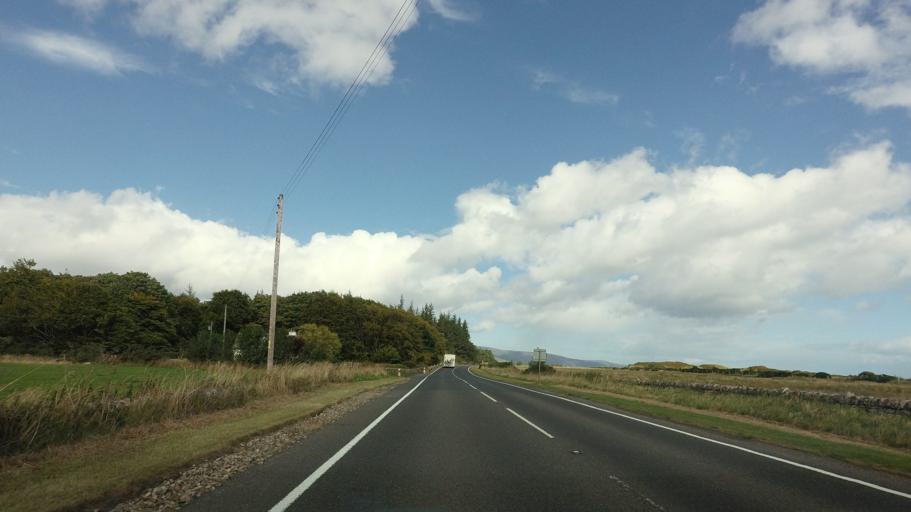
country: GB
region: Scotland
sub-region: Highland
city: Brora
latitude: 57.9915
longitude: -3.8937
